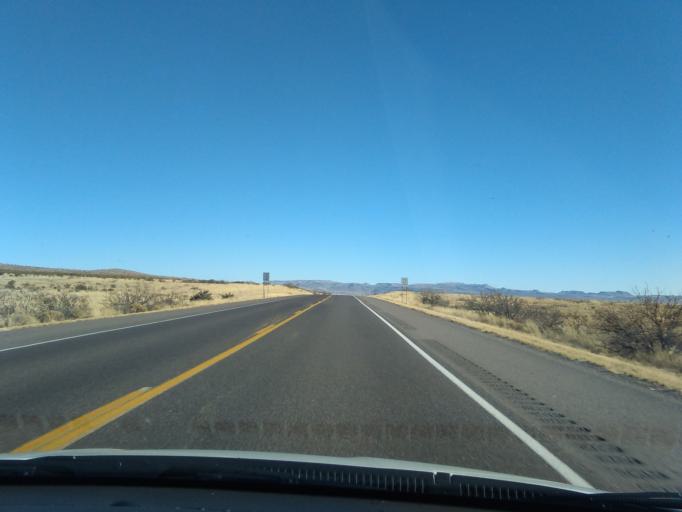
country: US
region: New Mexico
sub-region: Dona Ana County
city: Hatch
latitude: 32.5776
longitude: -107.4414
